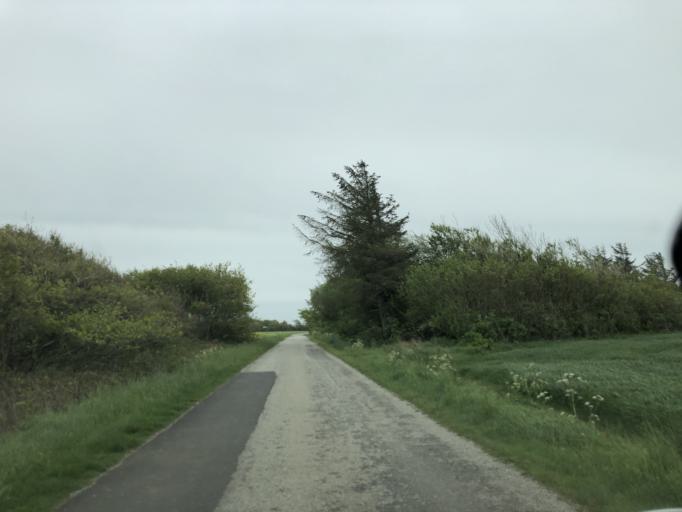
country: DK
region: Central Jutland
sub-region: Holstebro Kommune
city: Ulfborg
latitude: 56.2726
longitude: 8.1794
